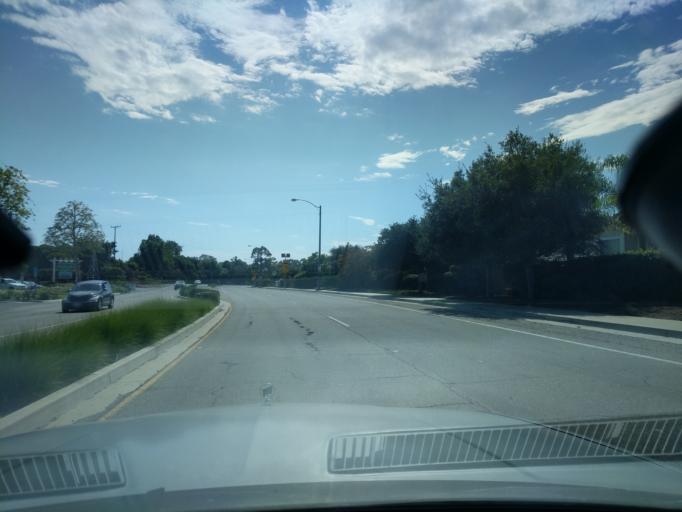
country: US
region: California
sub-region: Santa Barbara County
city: Goleta
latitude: 34.4435
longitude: -119.8103
